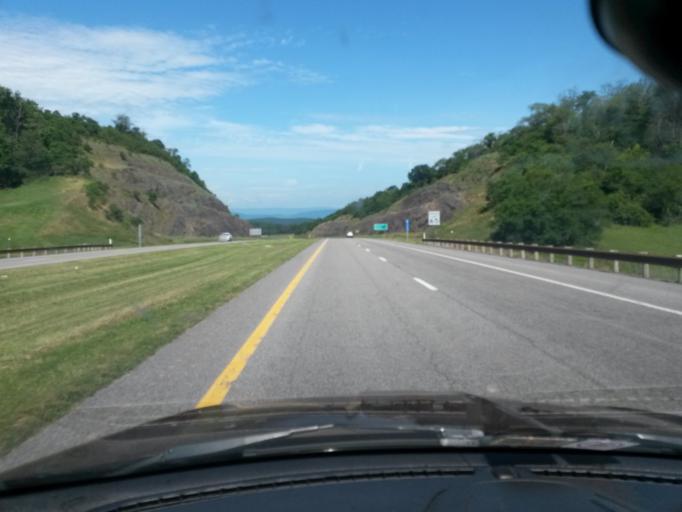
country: US
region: West Virginia
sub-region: Hardy County
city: Moorefield
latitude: 39.1019
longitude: -78.8430
